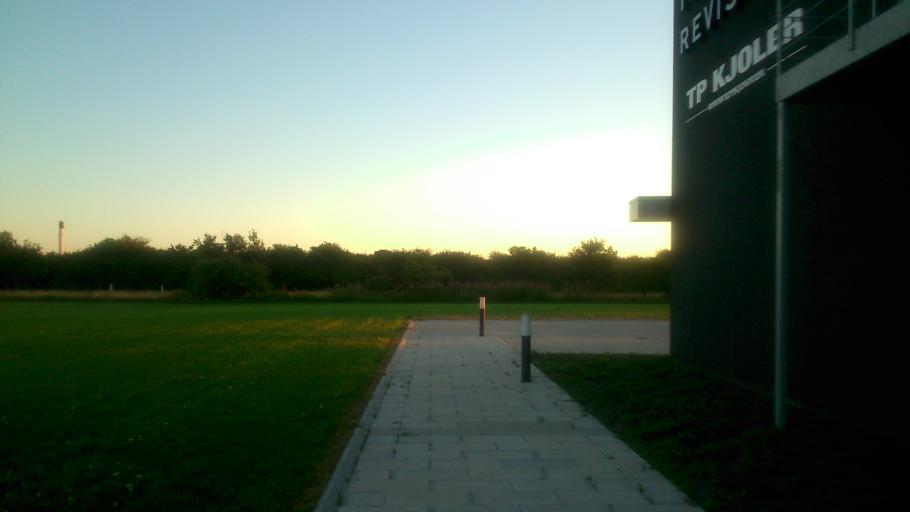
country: DK
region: Central Jutland
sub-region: Ringkobing-Skjern Kommune
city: Skjern
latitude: 55.9319
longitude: 8.4971
